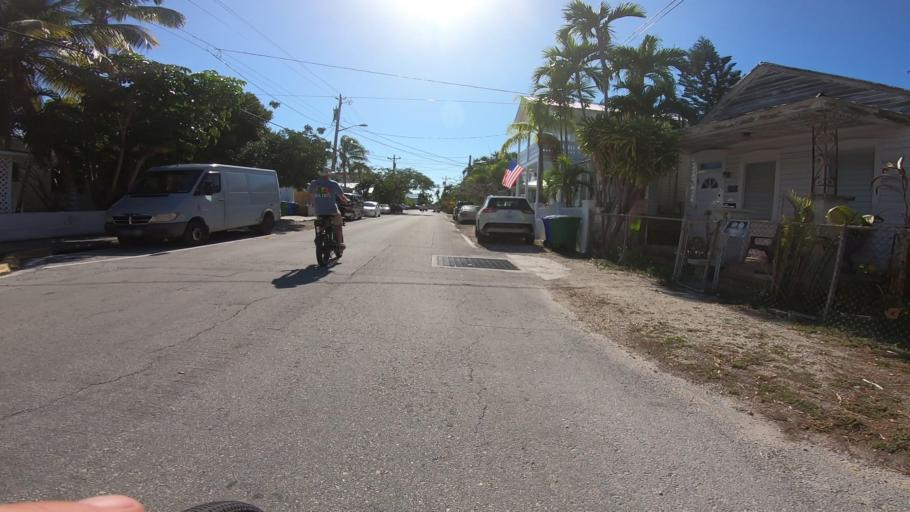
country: US
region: Florida
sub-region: Monroe County
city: Key West
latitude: 24.5517
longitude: -81.7939
